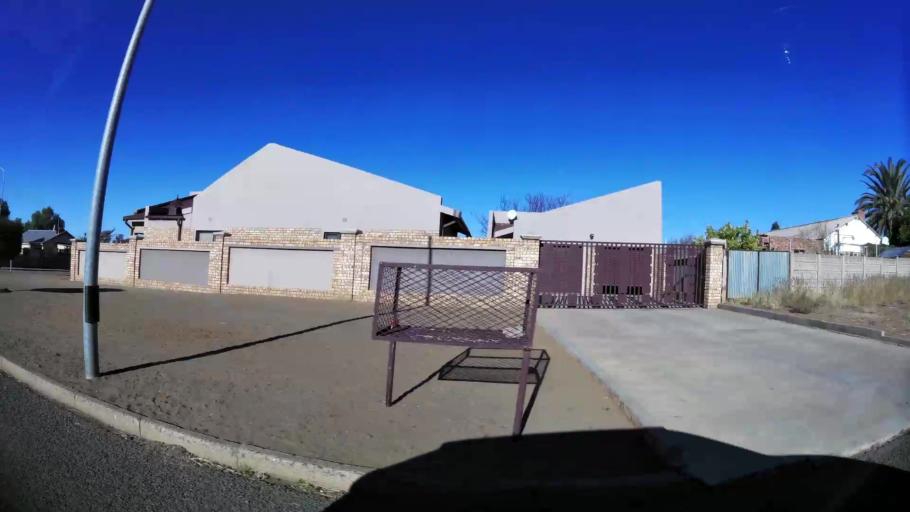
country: ZA
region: Northern Cape
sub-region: Frances Baard District Municipality
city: Kimberley
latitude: -28.7580
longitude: 24.7760
